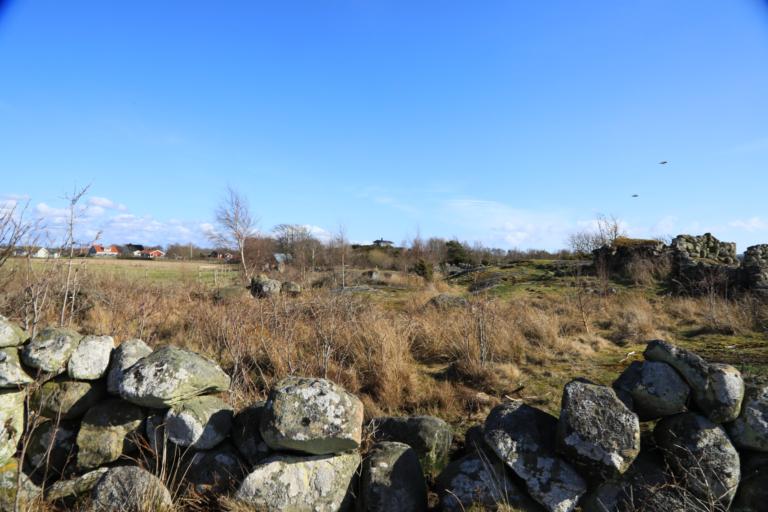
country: SE
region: Halland
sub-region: Varbergs Kommun
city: Varberg
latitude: 57.1227
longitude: 12.2078
